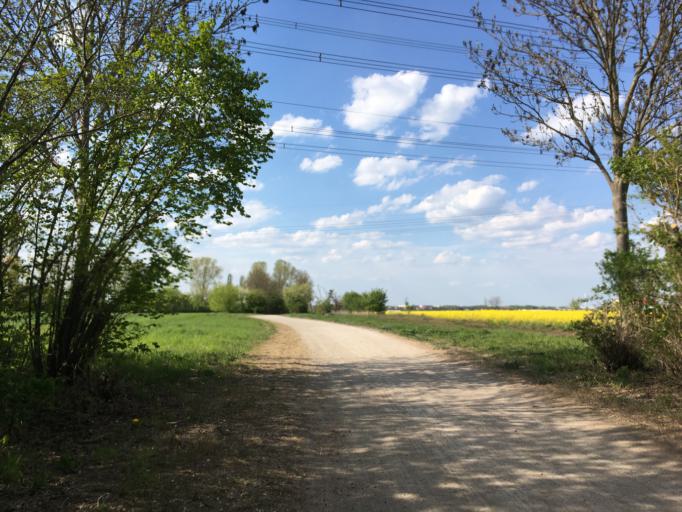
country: DE
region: Berlin
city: Wartenberg
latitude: 52.5940
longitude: 13.5067
